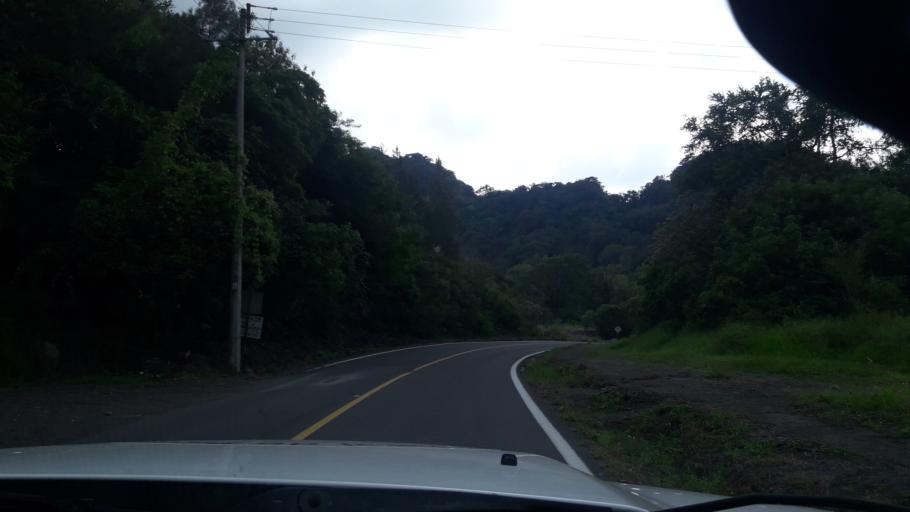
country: MX
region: Colima
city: Suchitlan
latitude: 19.4533
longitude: -103.7137
